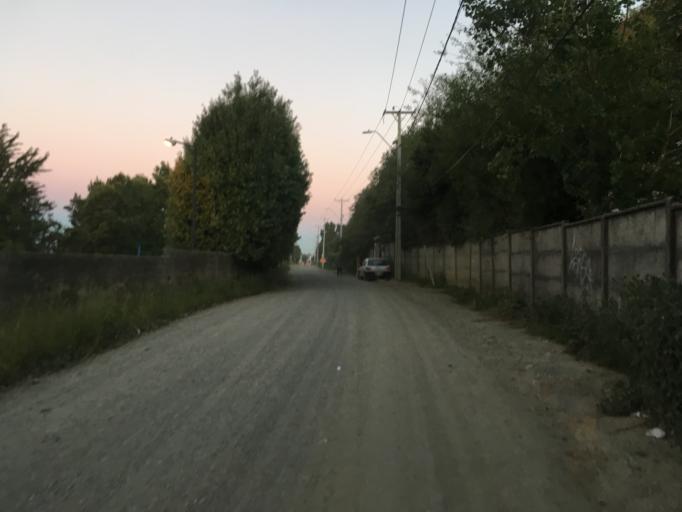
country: CL
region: Los Lagos
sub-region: Provincia de Chiloe
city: Ancud
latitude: -41.8609
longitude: -73.8252
